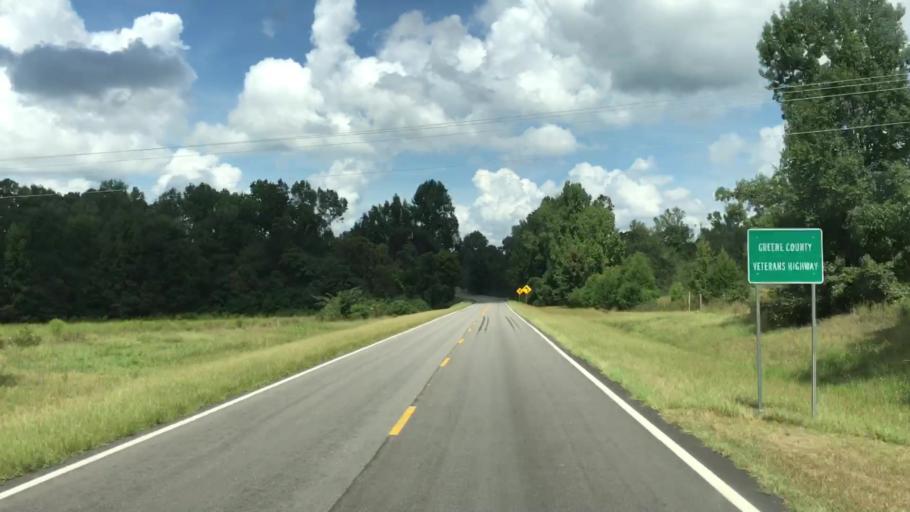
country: US
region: Georgia
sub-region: Greene County
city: Union Point
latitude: 33.5473
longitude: -83.0972
